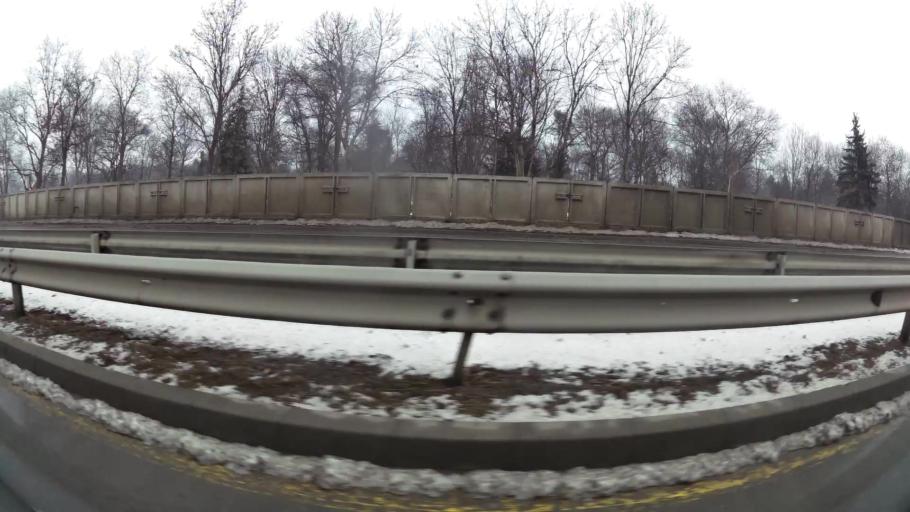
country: BG
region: Sofia-Capital
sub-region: Stolichna Obshtina
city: Sofia
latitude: 42.7136
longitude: 23.3287
